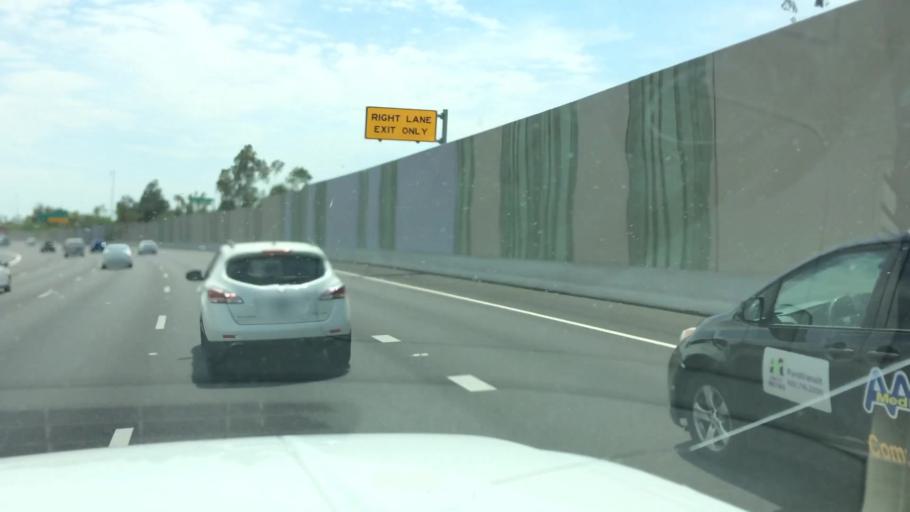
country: US
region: Arizona
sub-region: Maricopa County
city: Scottsdale
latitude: 33.5706
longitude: -111.8913
